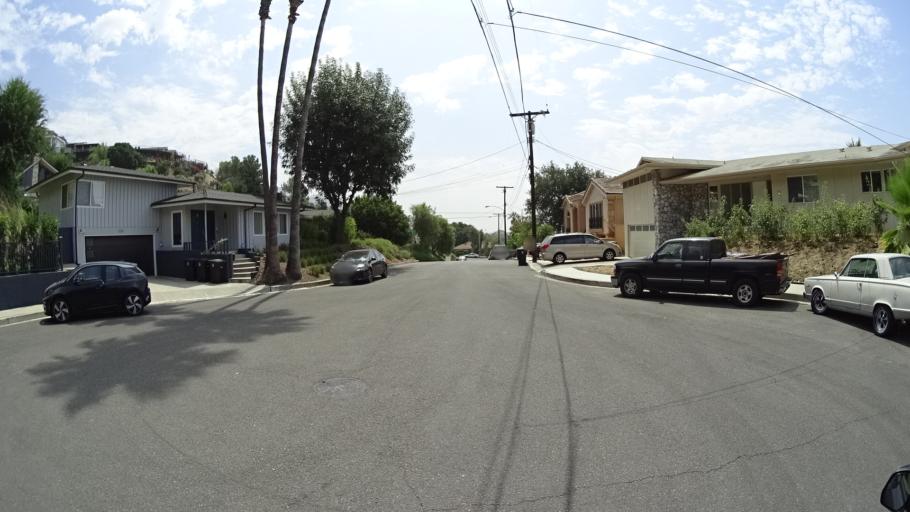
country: US
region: California
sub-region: Los Angeles County
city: Burbank
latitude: 34.1906
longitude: -118.2916
